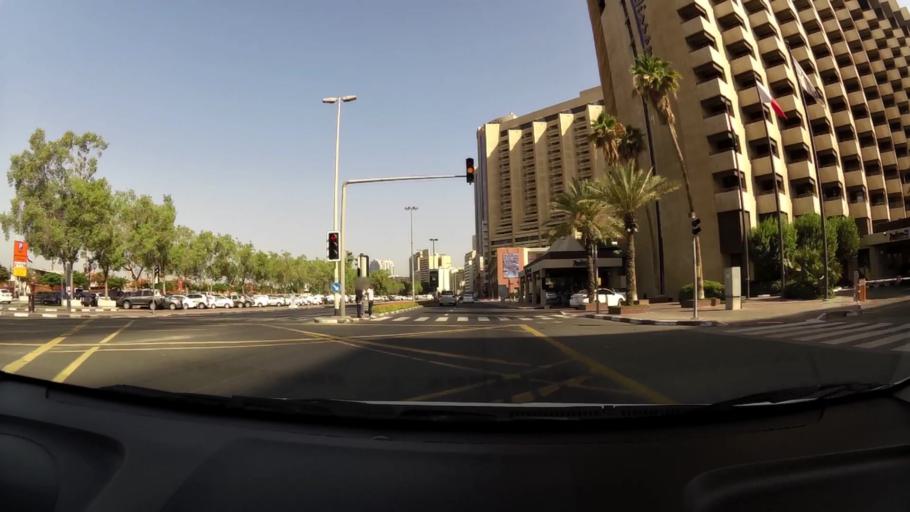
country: AE
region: Ash Shariqah
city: Sharjah
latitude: 25.2644
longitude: 55.3110
